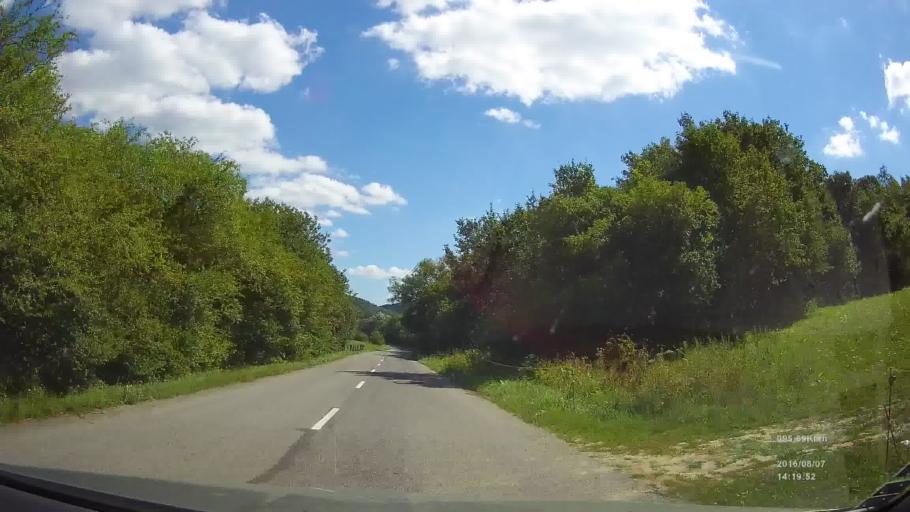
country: SK
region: Presovsky
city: Stropkov
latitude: 49.2976
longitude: 21.7566
